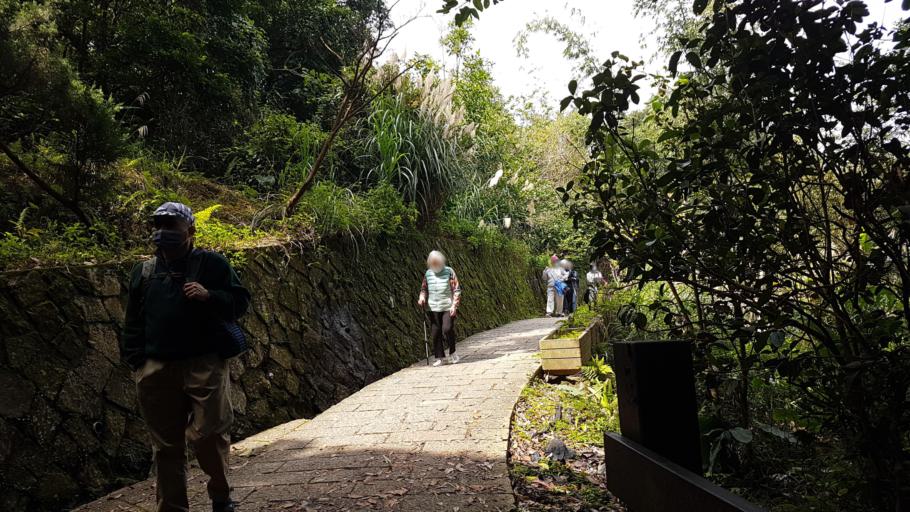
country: TW
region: Taipei
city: Taipei
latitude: 24.9677
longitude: 121.5817
